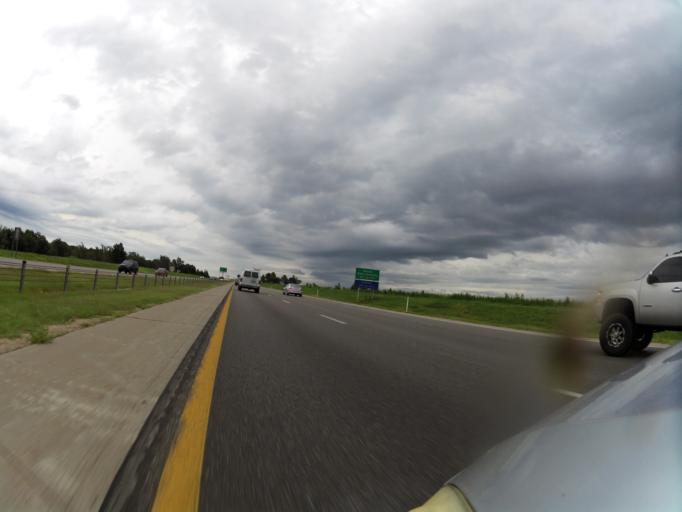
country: US
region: Kansas
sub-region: Sedgwick County
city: Bellaire
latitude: 37.7435
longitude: -97.3081
